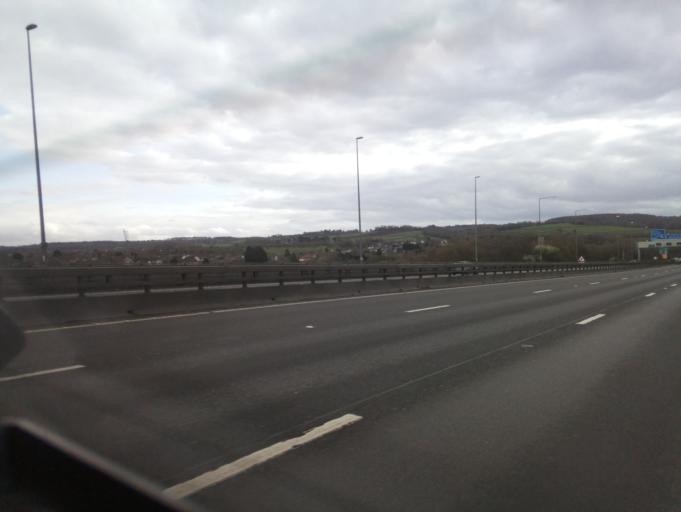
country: GB
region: England
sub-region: North Somerset
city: Easton-in-Gordano
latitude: 51.4856
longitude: -2.6959
